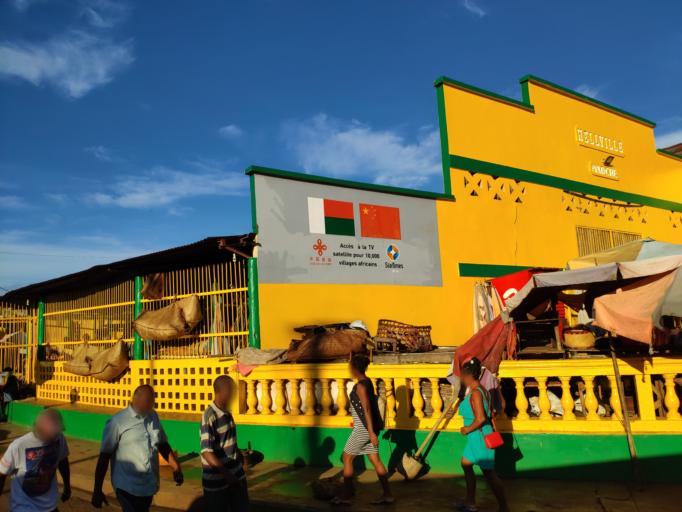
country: MG
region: Diana
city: Hell-Ville
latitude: -13.4014
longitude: 48.2719
